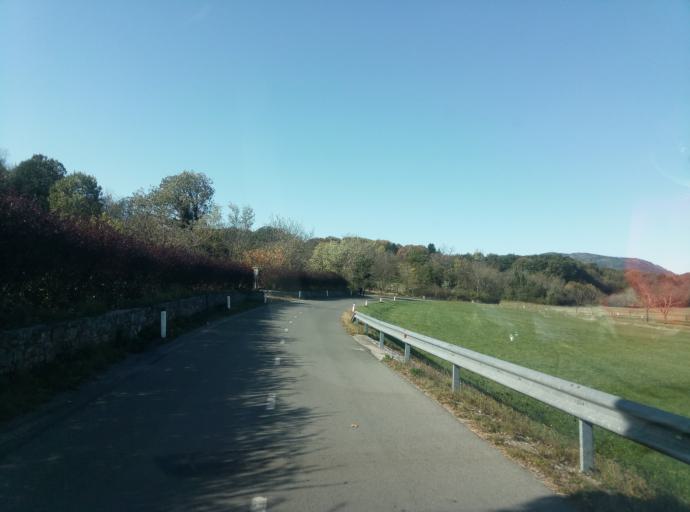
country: SI
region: Komen
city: Komen
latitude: 45.8200
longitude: 13.7476
